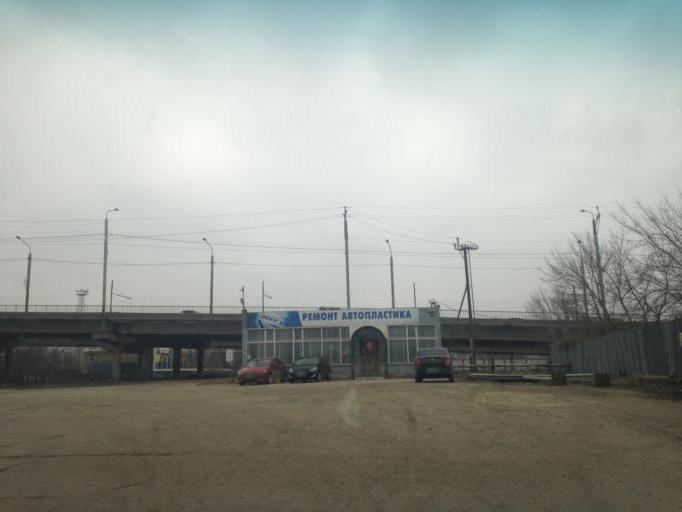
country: RU
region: Ulyanovsk
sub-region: Ulyanovskiy Rayon
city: Ulyanovsk
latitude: 54.3055
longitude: 48.3082
